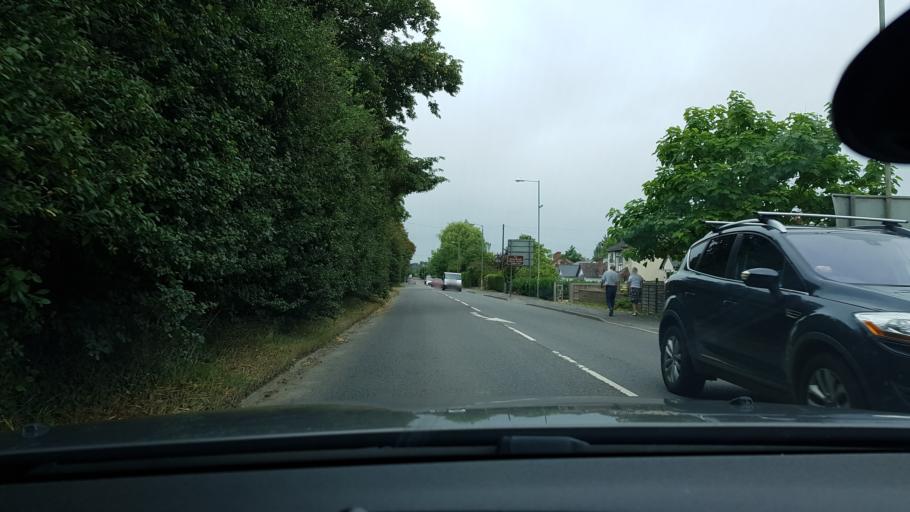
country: GB
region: England
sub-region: Wiltshire
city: Calne
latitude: 51.4260
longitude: -1.9785
